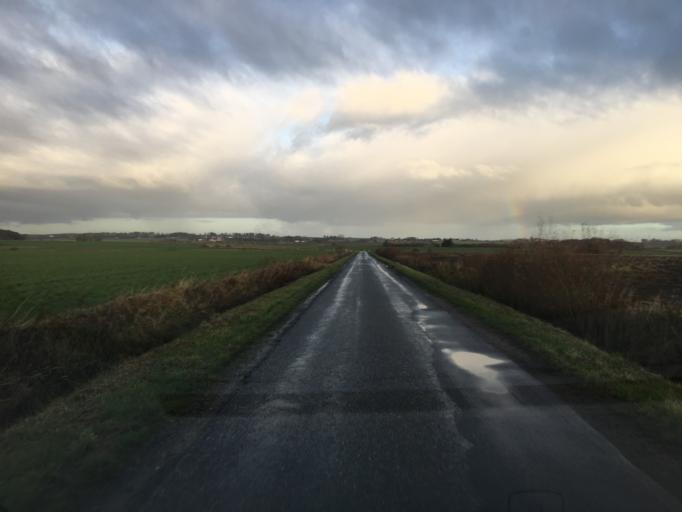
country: DK
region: South Denmark
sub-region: Tonder Kommune
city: Sherrebek
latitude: 55.1382
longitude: 8.8275
